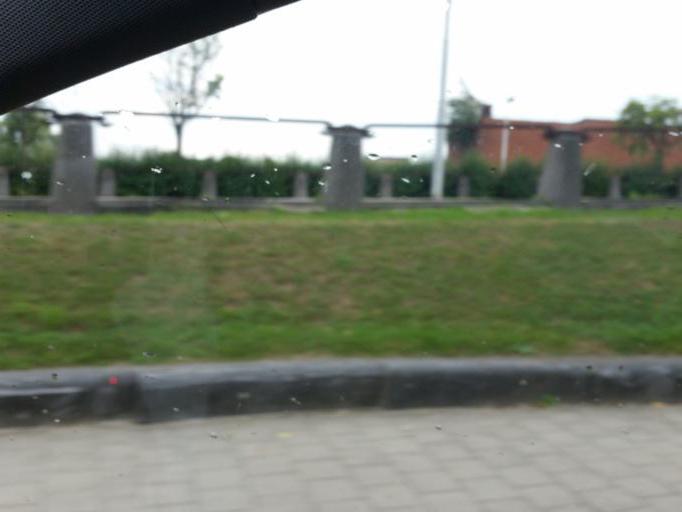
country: BE
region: Flanders
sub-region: Provincie Oost-Vlaanderen
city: Ledeberg
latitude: 51.0473
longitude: 3.7548
